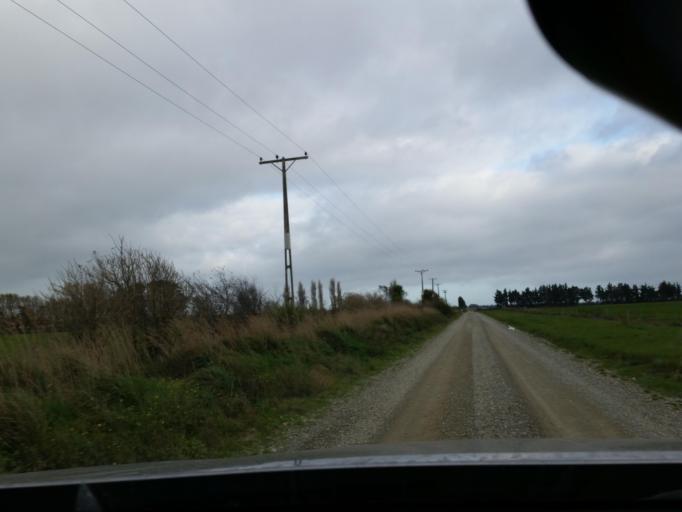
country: NZ
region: Southland
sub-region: Southland District
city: Winton
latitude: -46.2324
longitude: 168.3672
